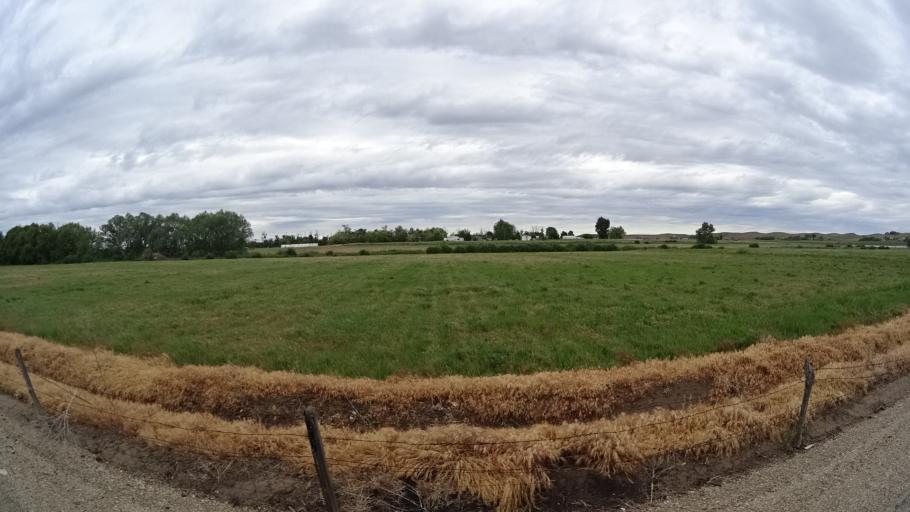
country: US
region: Idaho
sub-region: Ada County
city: Eagle
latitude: 43.7230
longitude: -116.4133
